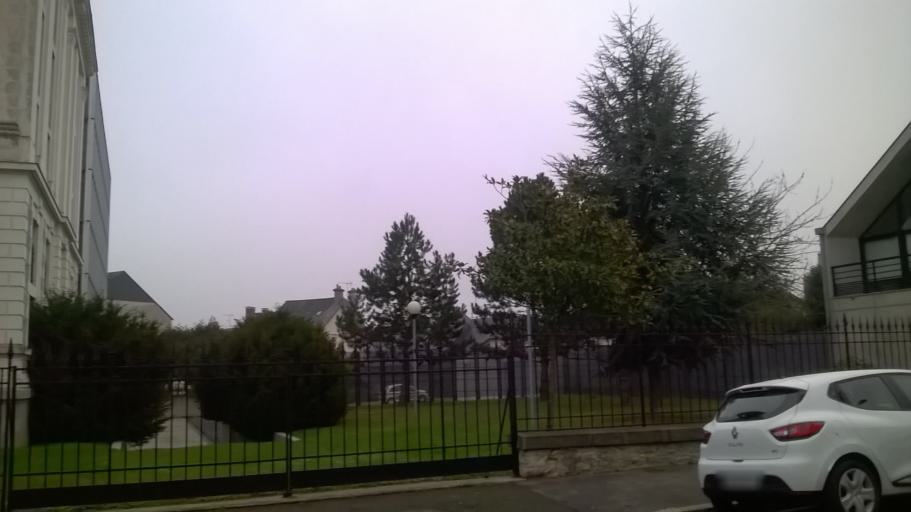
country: FR
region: Pays de la Loire
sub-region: Departement de la Mayenne
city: Laval
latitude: 48.0726
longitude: -0.7582
